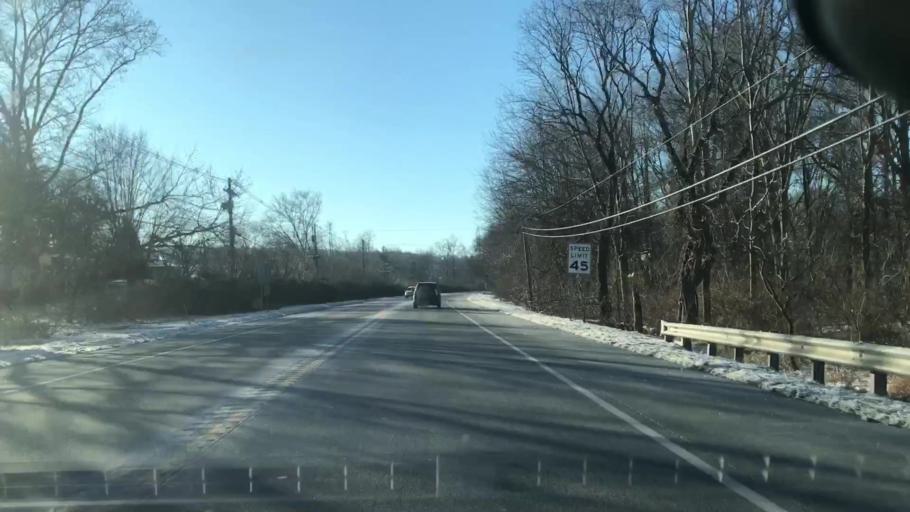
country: US
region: New Jersey
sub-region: Morris County
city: Chester
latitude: 40.8293
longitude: -74.7087
